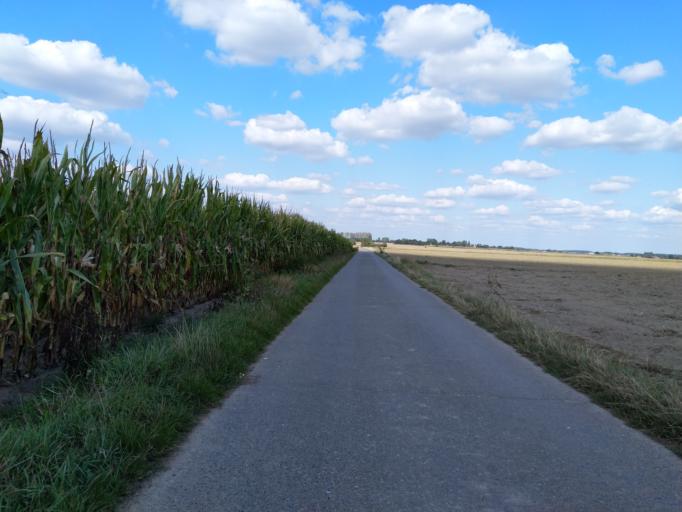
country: BE
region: Wallonia
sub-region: Province du Hainaut
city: Saint-Ghislain
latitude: 50.5122
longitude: 3.8197
